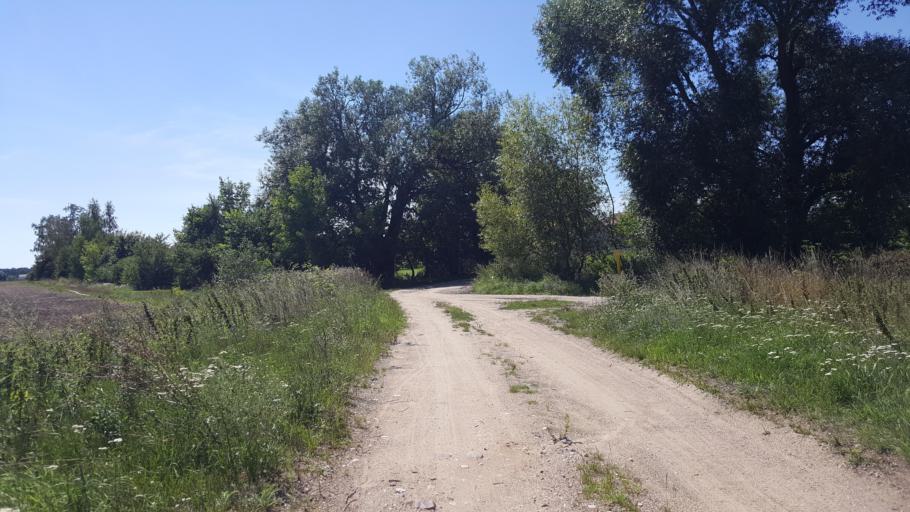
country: BY
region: Brest
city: Charnawchytsy
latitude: 52.2353
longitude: 23.7851
